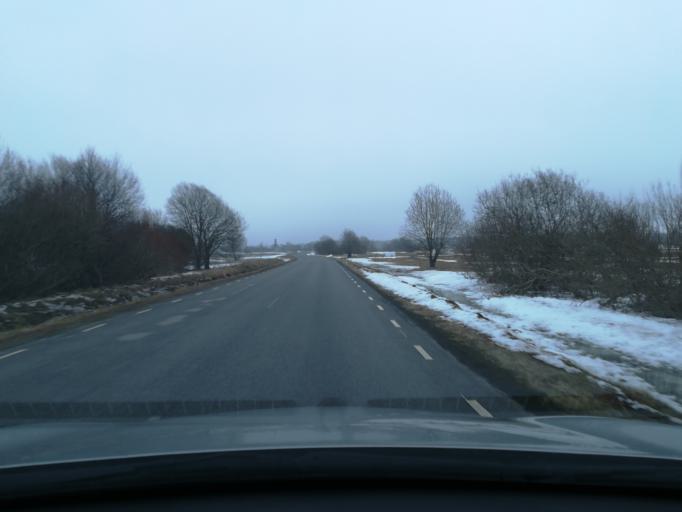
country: EE
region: Harju
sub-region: Kuusalu vald
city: Kuusalu
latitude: 59.4733
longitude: 25.5495
